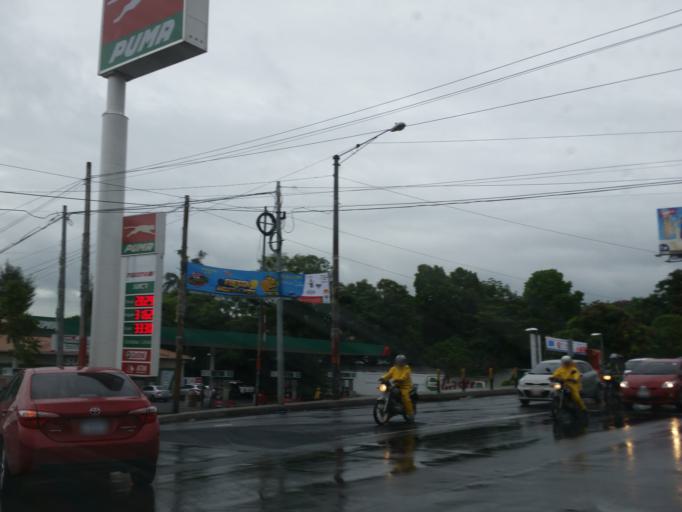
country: NI
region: Managua
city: Managua
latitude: 12.0978
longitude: -86.2411
